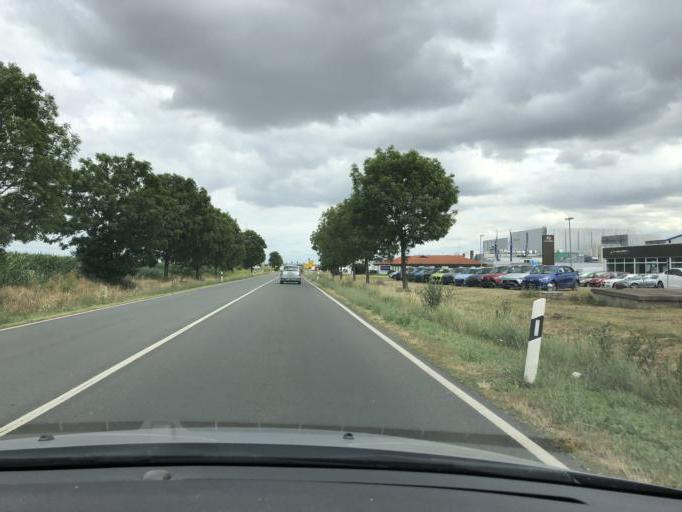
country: DE
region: Saxony-Anhalt
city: Erdeborn
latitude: 51.5079
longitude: 11.5878
